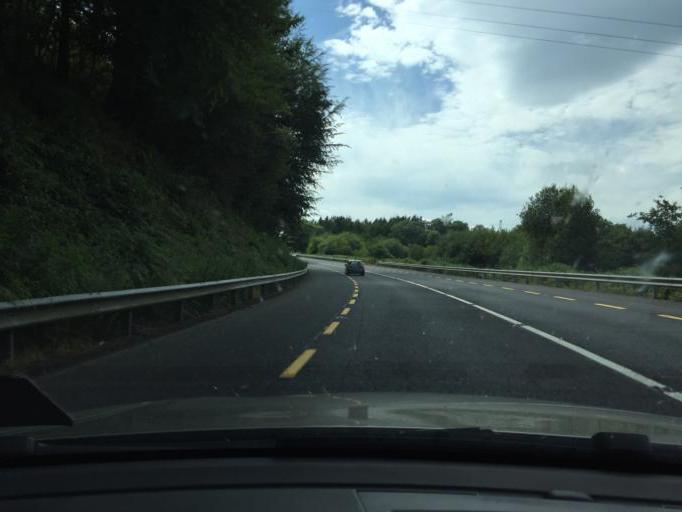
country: IE
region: Leinster
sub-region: Kilkenny
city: Mooncoin
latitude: 52.2380
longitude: -7.2798
